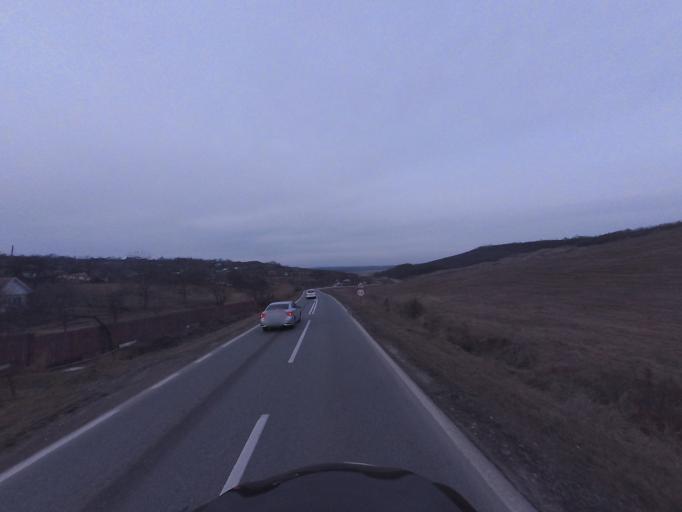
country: RO
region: Iasi
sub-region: Comuna Popricani
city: Popricani
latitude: 47.2936
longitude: 27.5105
